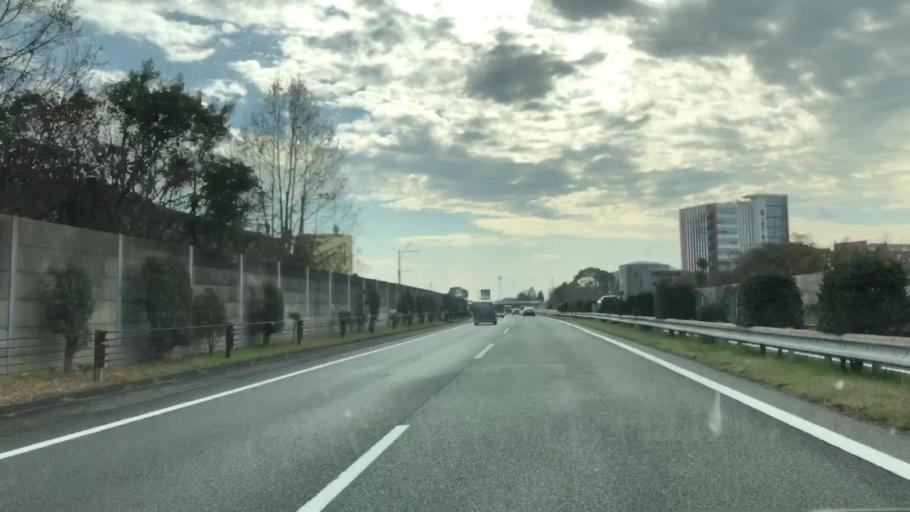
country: JP
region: Fukuoka
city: Kurume
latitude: 33.2683
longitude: 130.5395
